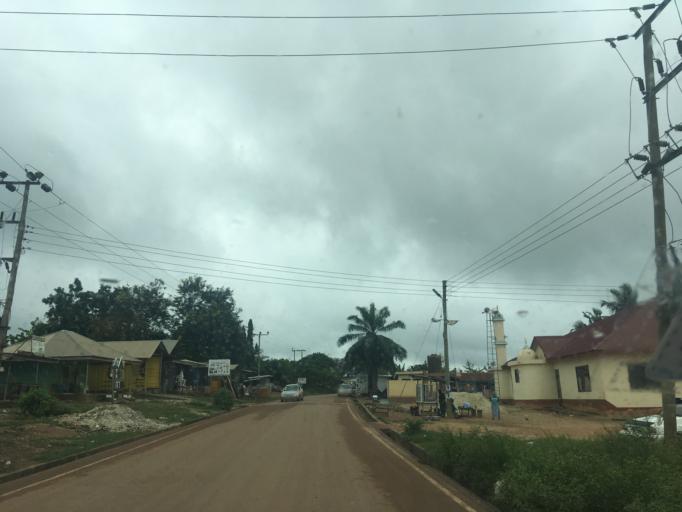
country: GH
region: Western
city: Wassa-Akropong
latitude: 5.8155
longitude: -2.4341
